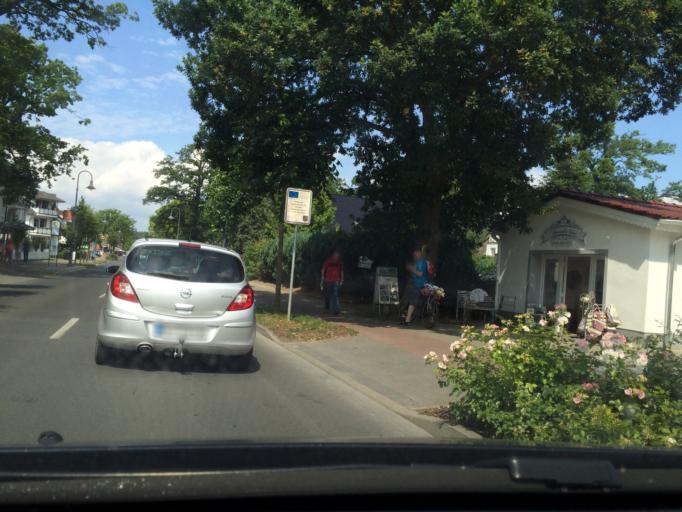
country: DE
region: Mecklenburg-Vorpommern
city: Ostseebad Binz
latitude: 54.4000
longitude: 13.6097
